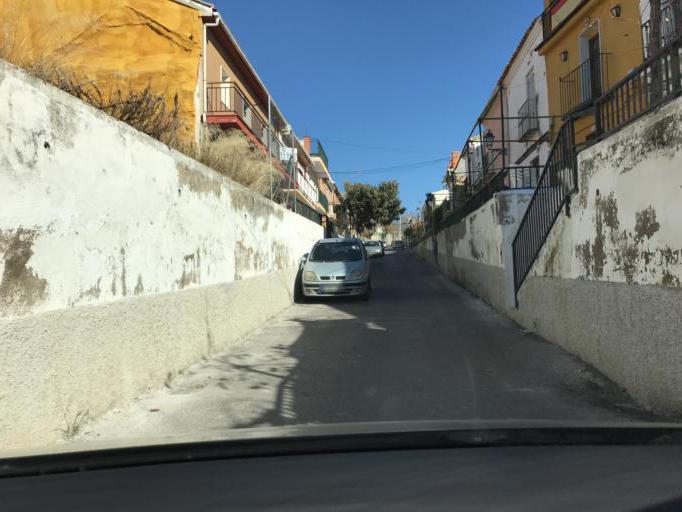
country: ES
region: Andalusia
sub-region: Provincia de Granada
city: Viznar
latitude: 37.2078
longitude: -3.5593
